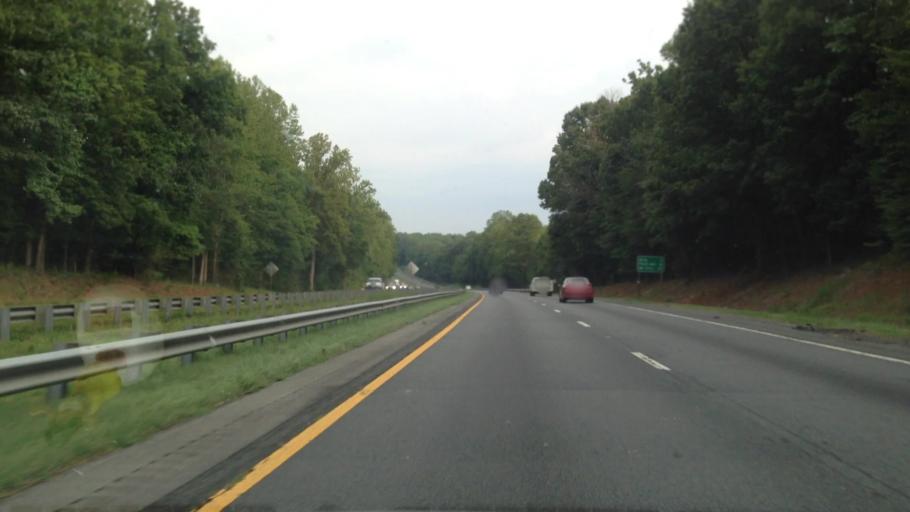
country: US
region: North Carolina
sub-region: Forsyth County
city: Rural Hall
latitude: 36.2205
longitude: -80.3120
